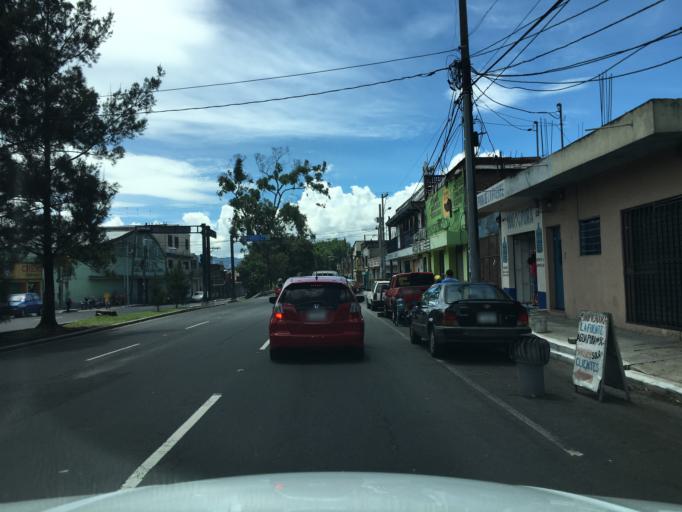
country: GT
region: Guatemala
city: Guatemala City
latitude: 14.6232
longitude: -90.5408
